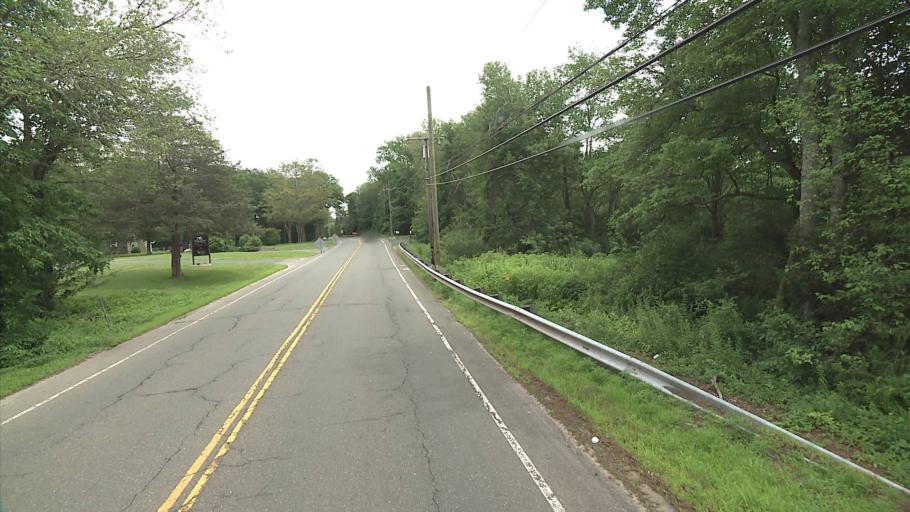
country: US
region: Connecticut
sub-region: Middlesex County
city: Clinton
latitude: 41.3570
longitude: -72.5597
